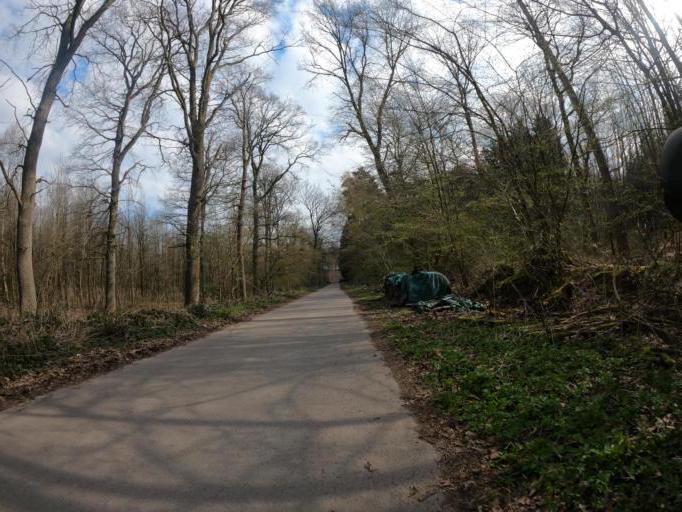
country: DE
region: North Rhine-Westphalia
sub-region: Regierungsbezirk Koln
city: Aachen
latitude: 50.7264
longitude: 6.1070
